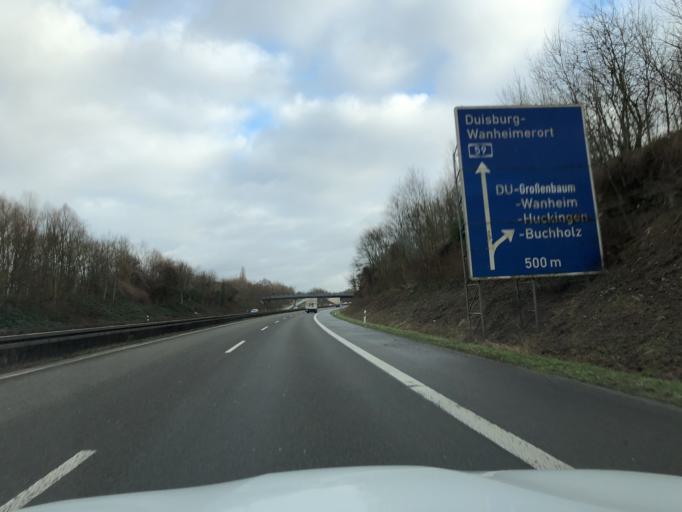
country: DE
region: North Rhine-Westphalia
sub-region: Regierungsbezirk Dusseldorf
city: Hochfeld
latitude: 51.3658
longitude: 6.7692
